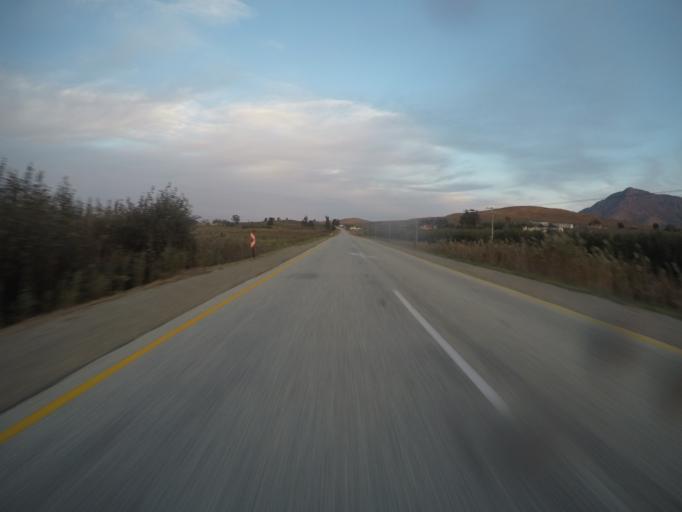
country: ZA
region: Western Cape
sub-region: Eden District Municipality
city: Plettenberg Bay
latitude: -33.7335
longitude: 23.4045
